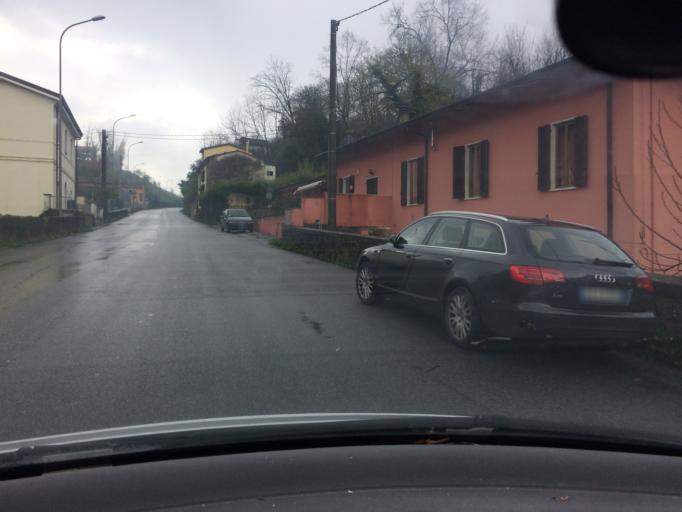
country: IT
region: Tuscany
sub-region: Provincia di Massa-Carrara
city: Massa
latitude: 44.0685
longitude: 10.1094
